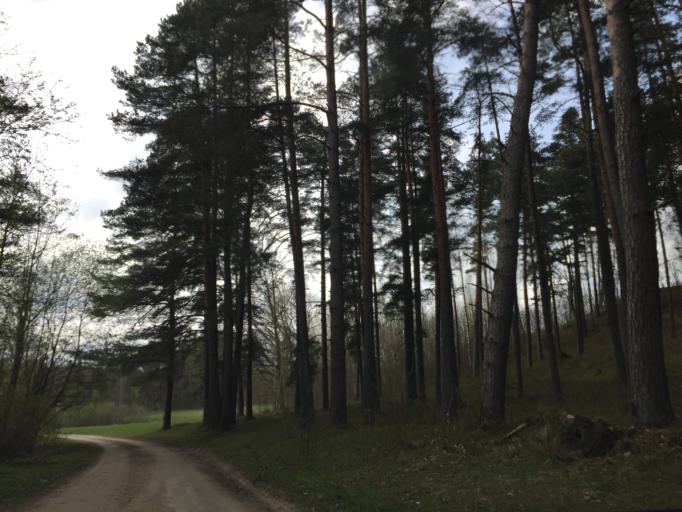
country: LV
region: Plavinu
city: Plavinas
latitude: 56.6175
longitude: 25.6975
